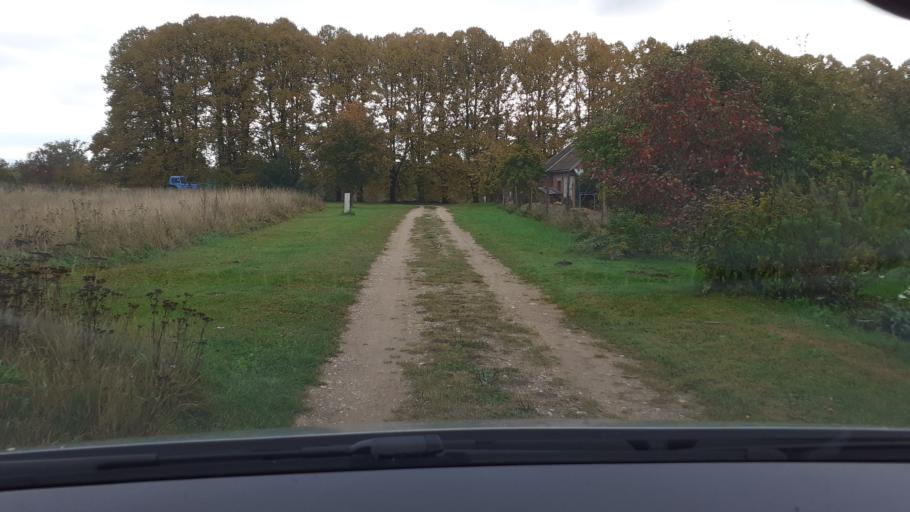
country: LV
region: Kuldigas Rajons
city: Kuldiga
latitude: 57.0168
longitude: 21.9054
